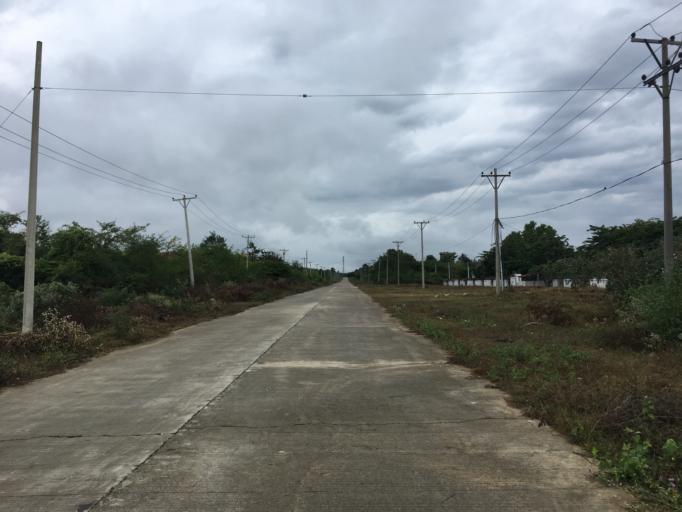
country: MM
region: Mandalay
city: Nay Pyi Taw
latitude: 19.6989
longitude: 96.1187
